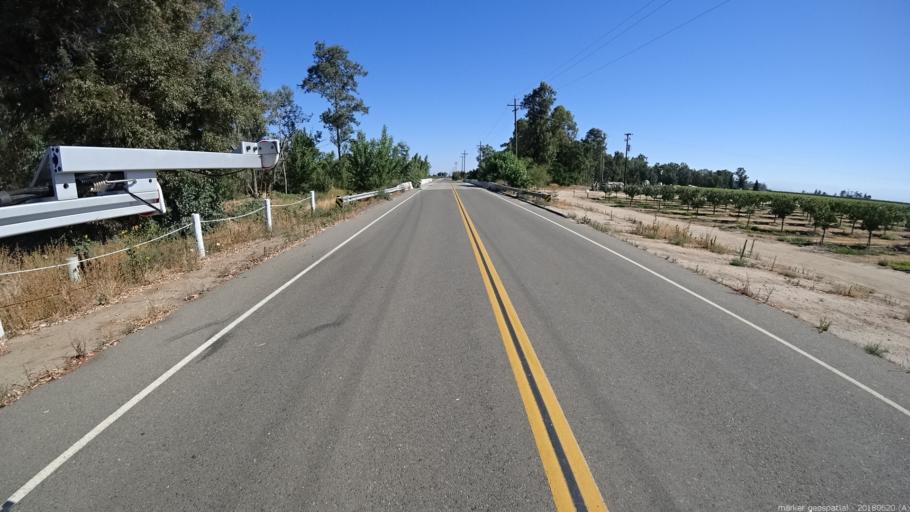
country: US
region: California
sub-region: Madera County
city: Parkwood
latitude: 36.9014
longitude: -120.0376
